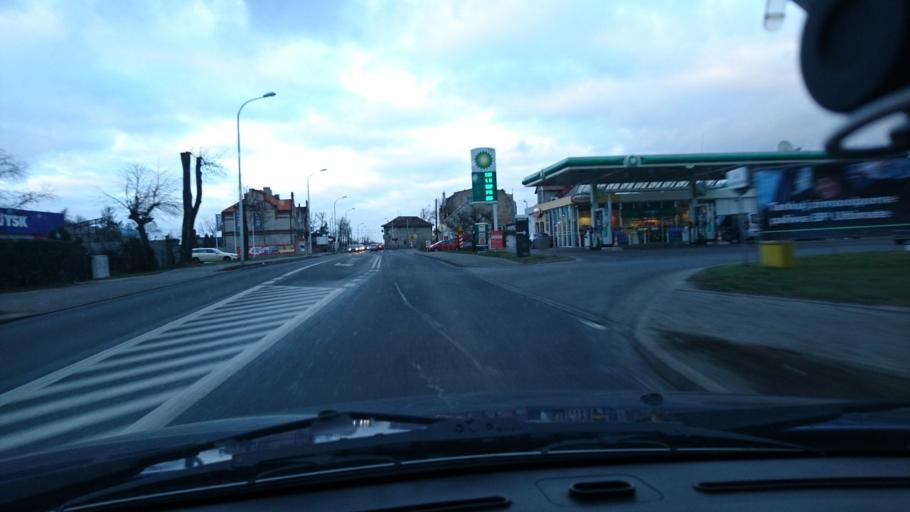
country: PL
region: Greater Poland Voivodeship
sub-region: Powiat kepinski
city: Kepno
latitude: 51.2885
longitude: 17.9933
